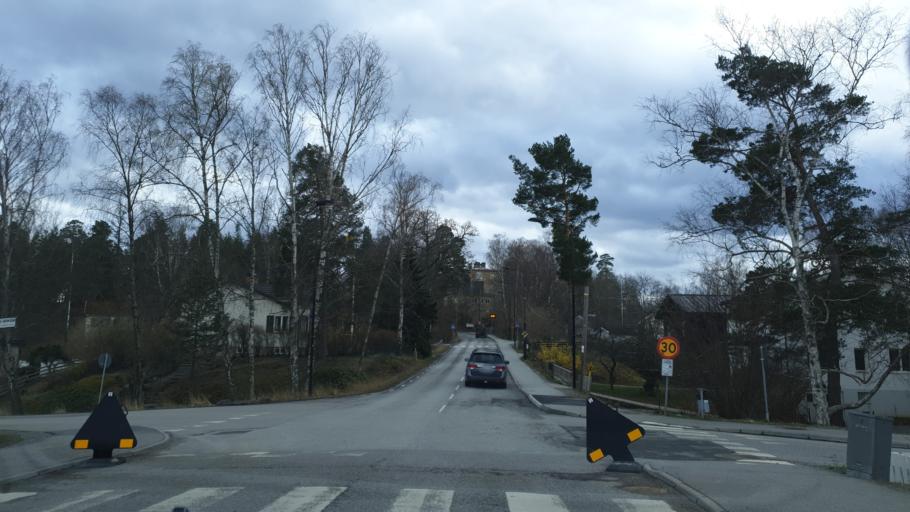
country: SE
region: Stockholm
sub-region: Nacka Kommun
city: Nacka
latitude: 59.3079
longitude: 18.2006
